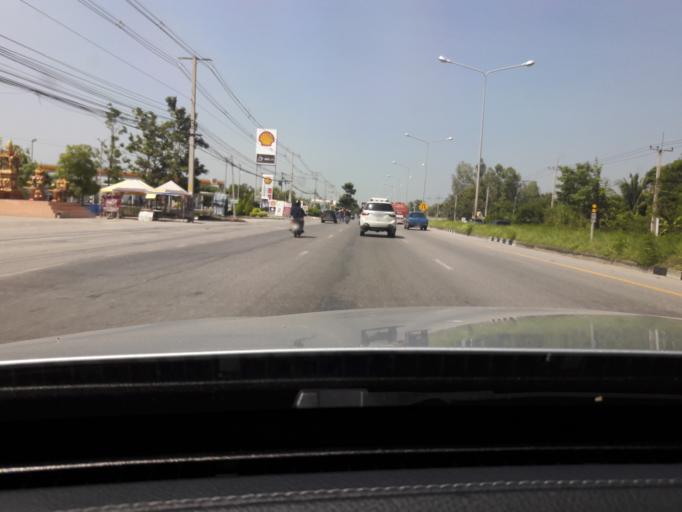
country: TH
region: Phetchaburi
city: Cha-am
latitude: 12.8628
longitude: 99.9206
